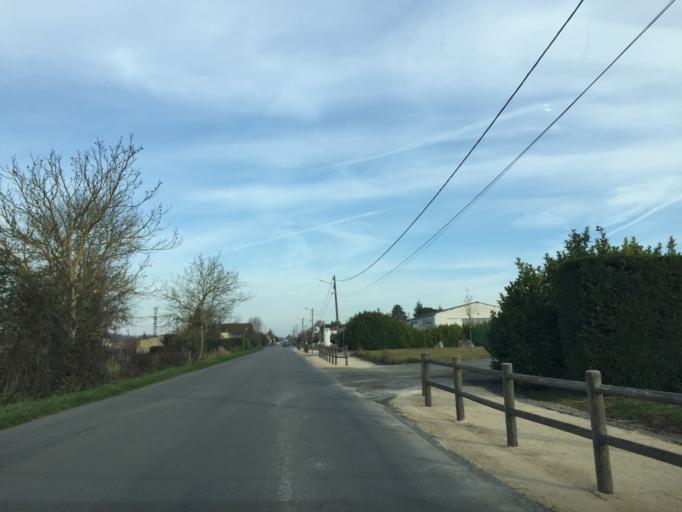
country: FR
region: Poitou-Charentes
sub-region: Departement de la Charente
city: Chalais
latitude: 45.2635
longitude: 0.0417
